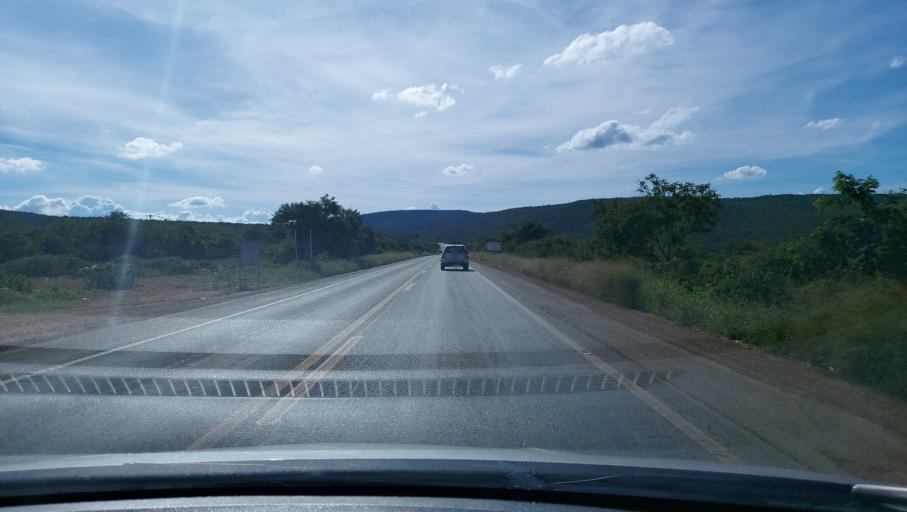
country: BR
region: Bahia
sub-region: Seabra
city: Seabra
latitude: -12.4577
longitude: -41.6483
